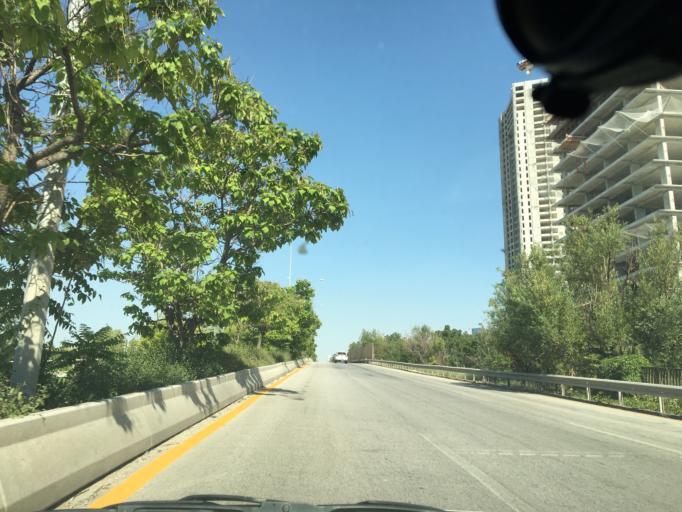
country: TR
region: Ankara
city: Ankara
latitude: 39.9180
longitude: 32.7885
